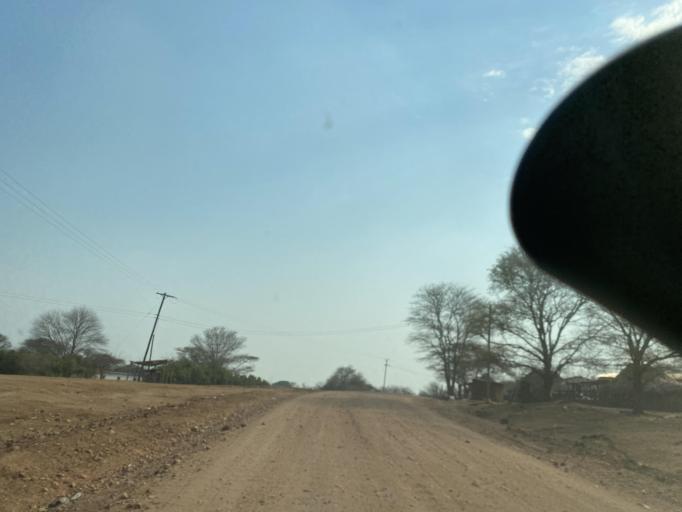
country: ZW
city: Chirundu
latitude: -15.9281
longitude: 28.9693
